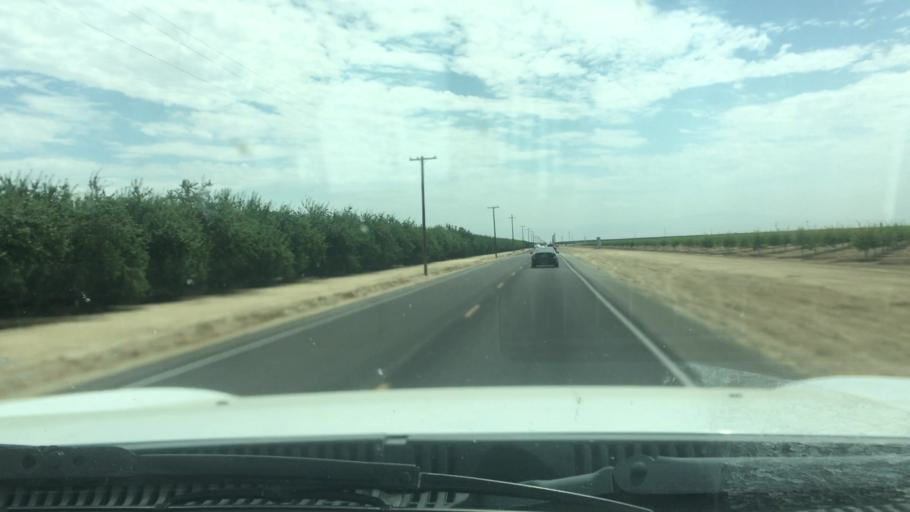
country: US
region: California
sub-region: Kern County
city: Wasco
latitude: 35.5581
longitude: -119.3027
